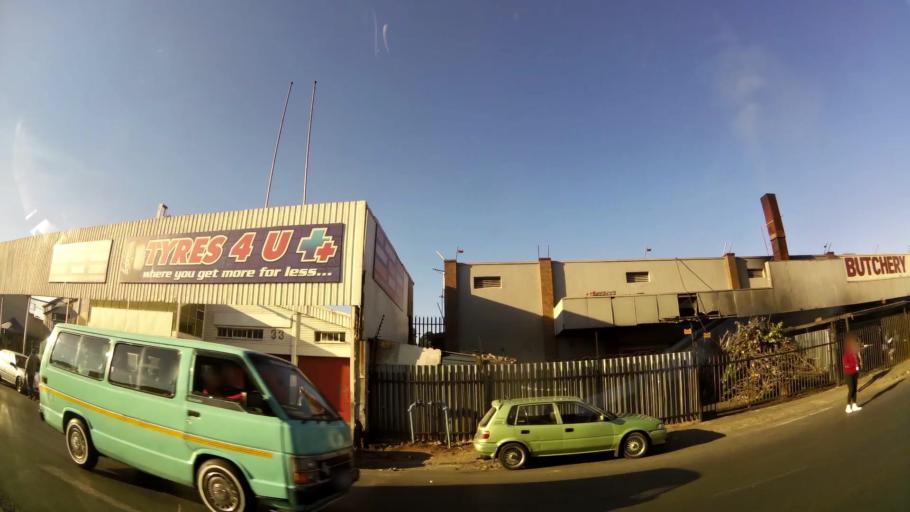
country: ZA
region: Gauteng
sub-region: City of Johannesburg Metropolitan Municipality
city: Roodepoort
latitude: -26.1601
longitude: 27.8693
